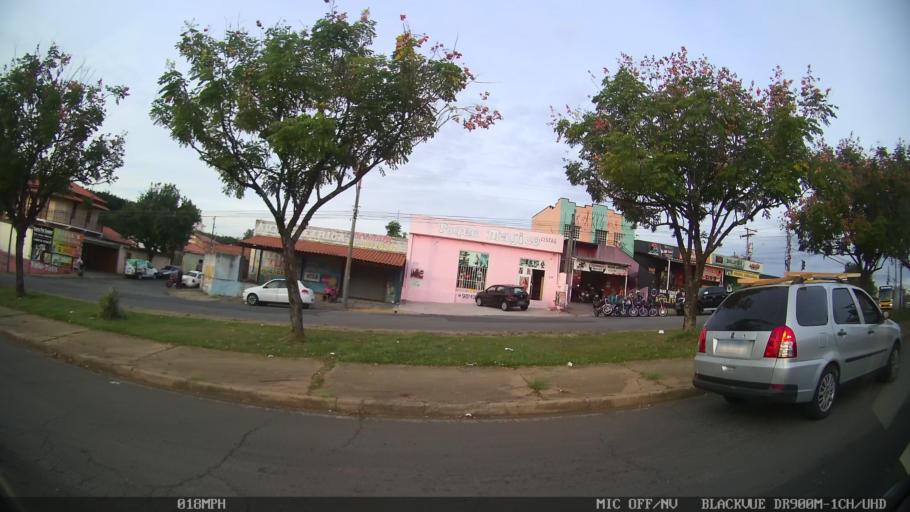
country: BR
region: Sao Paulo
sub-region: Limeira
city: Limeira
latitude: -22.5784
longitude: -47.3771
